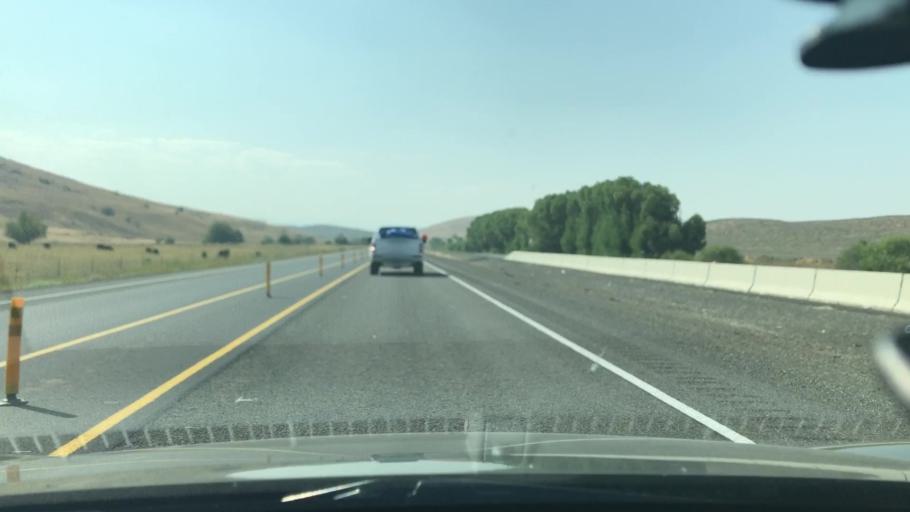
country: US
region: Oregon
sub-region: Baker County
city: Baker City
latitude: 44.6759
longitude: -117.6401
